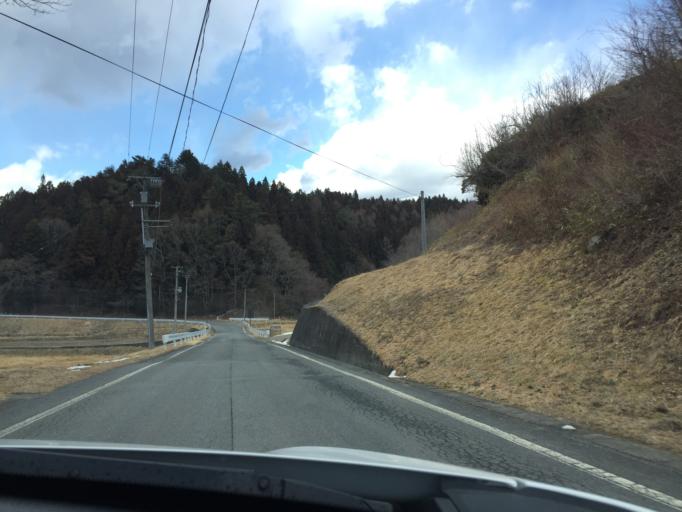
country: JP
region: Fukushima
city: Iwaki
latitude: 37.2406
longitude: 140.7278
